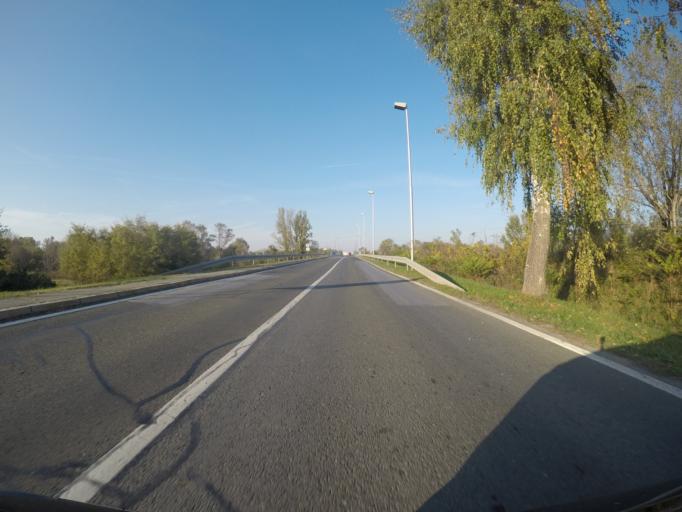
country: HU
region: Somogy
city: Barcs
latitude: 45.9435
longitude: 17.4612
